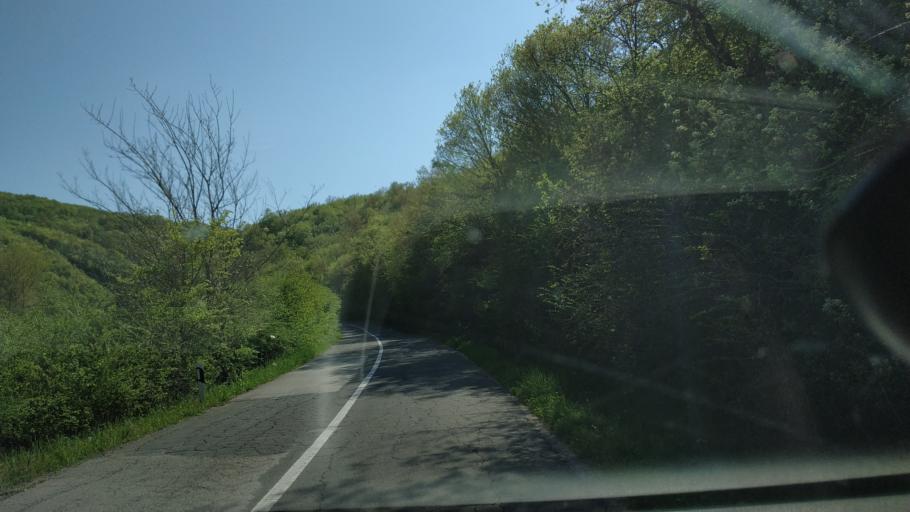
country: RS
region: Central Serbia
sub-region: Nisavski Okrug
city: Nis
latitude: 43.4106
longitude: 21.8246
